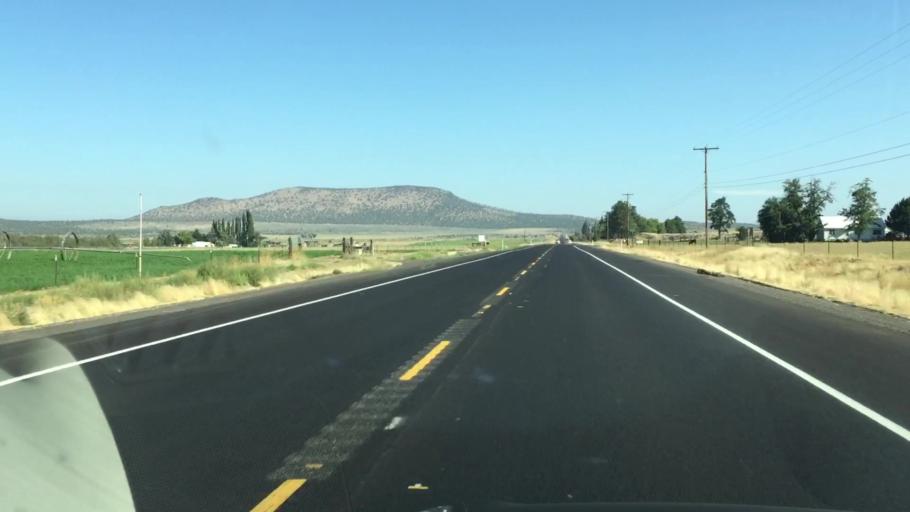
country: US
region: Oregon
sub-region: Deschutes County
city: Terrebonne
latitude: 44.4321
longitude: -121.1993
